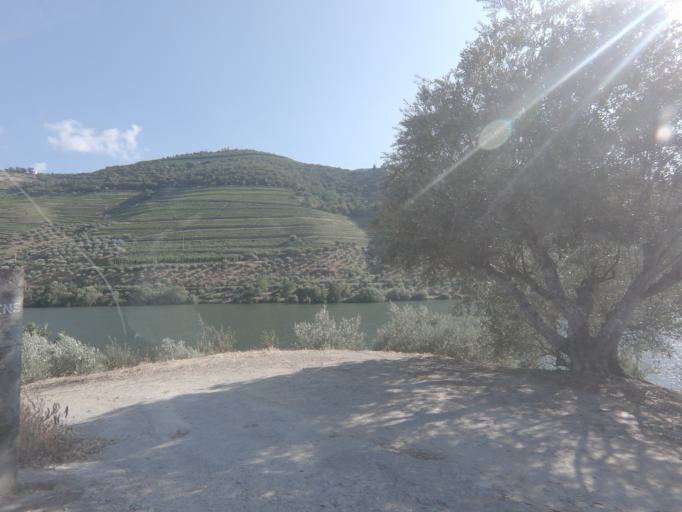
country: PT
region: Vila Real
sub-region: Sabrosa
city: Vilela
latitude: 41.1868
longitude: -7.5369
